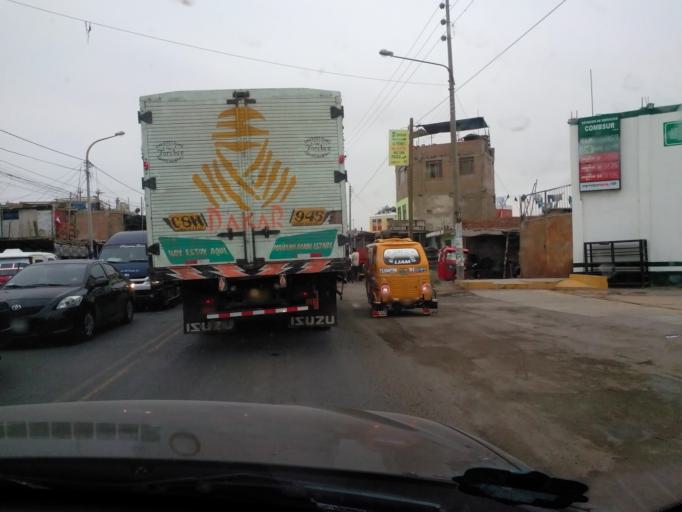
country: PE
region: Ica
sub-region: Provincia de Chincha
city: Chincha Alta
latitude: -13.4209
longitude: -76.1370
